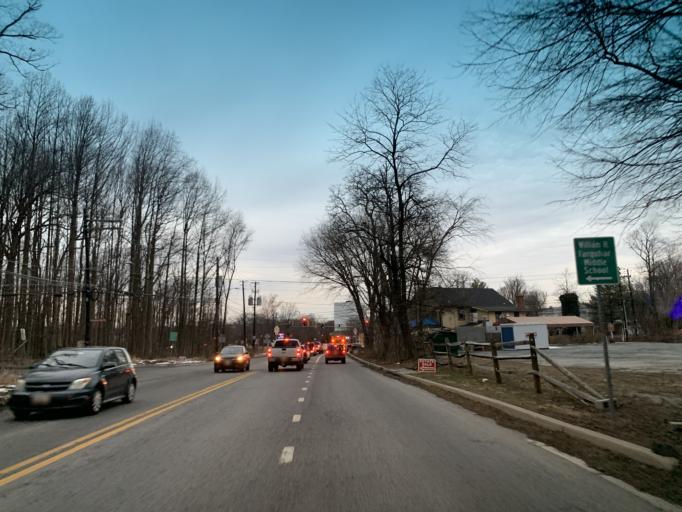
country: US
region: Maryland
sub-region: Montgomery County
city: Olney
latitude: 39.1436
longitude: -77.0424
